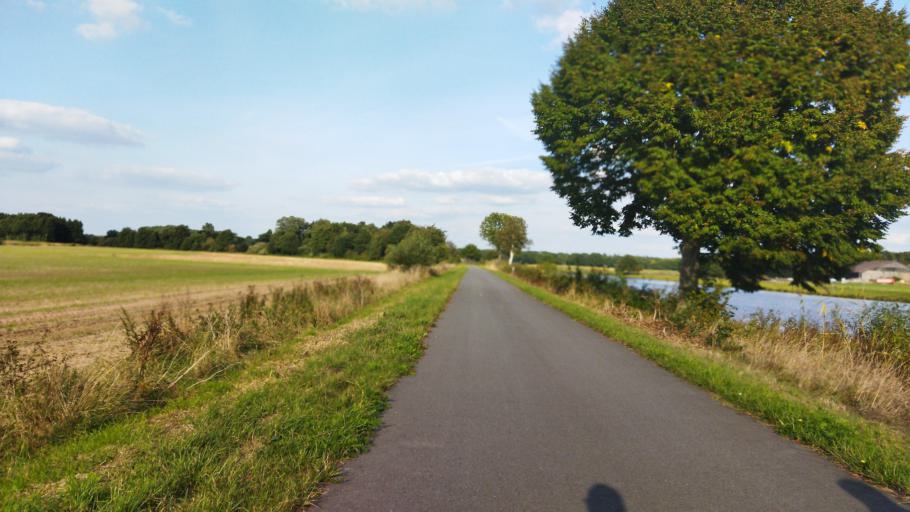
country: DE
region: Lower Saxony
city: Lehe
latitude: 53.0059
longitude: 7.3225
